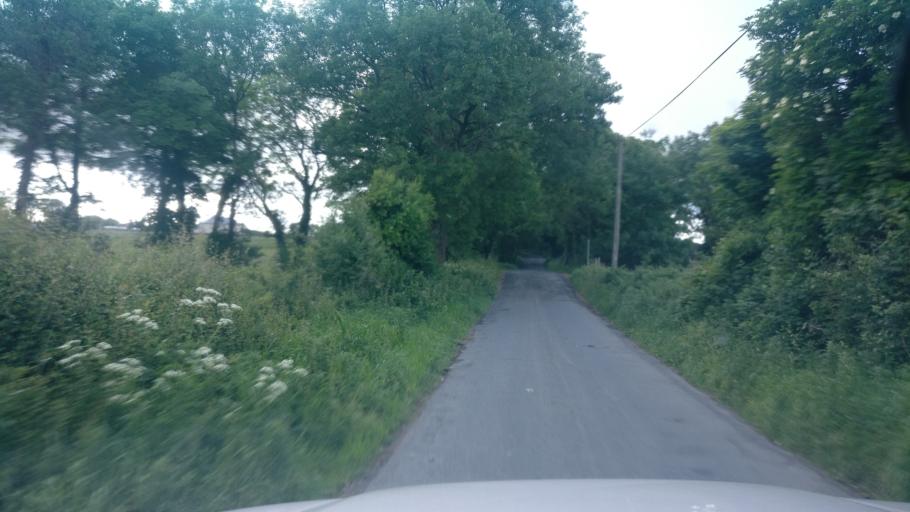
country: IE
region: Connaught
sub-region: County Galway
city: Ballinasloe
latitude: 53.2329
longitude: -8.1951
